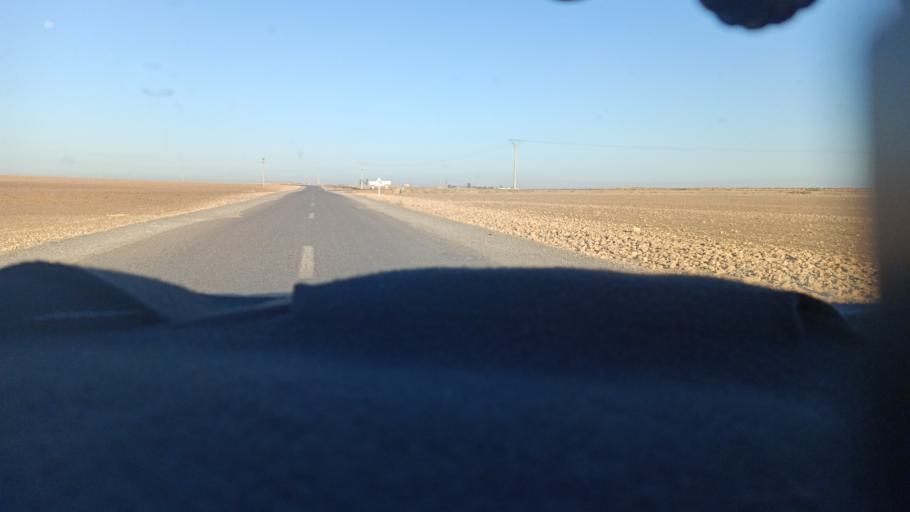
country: MA
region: Doukkala-Abda
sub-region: Safi
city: Youssoufia
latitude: 32.3702
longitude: -8.6286
